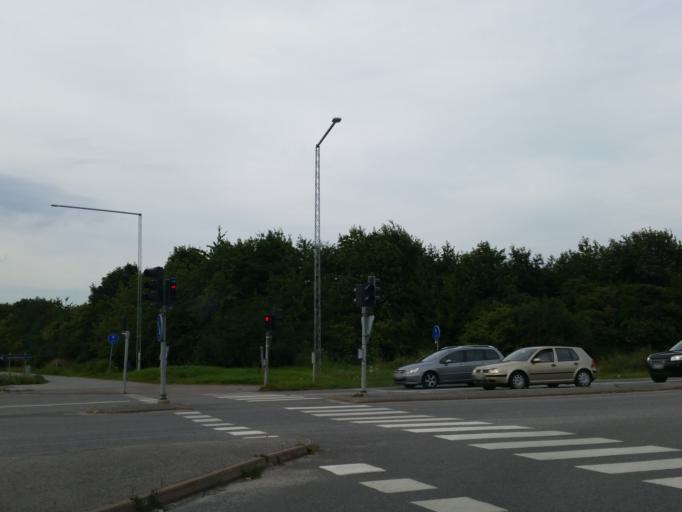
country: SE
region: Stockholm
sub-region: Jarfalla Kommun
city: Jakobsberg
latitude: 59.4223
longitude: 17.8560
